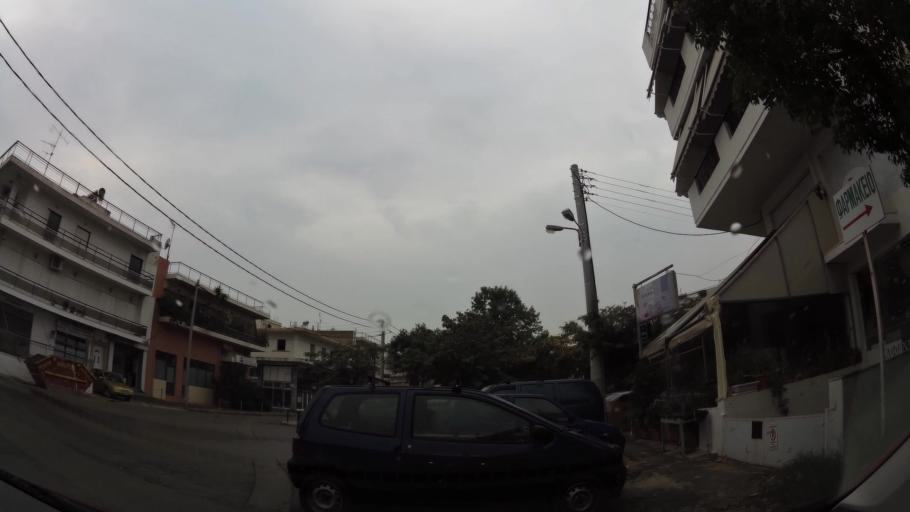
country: GR
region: Attica
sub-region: Nomarchia Athinas
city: Peristeri
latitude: 38.0147
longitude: 23.7100
